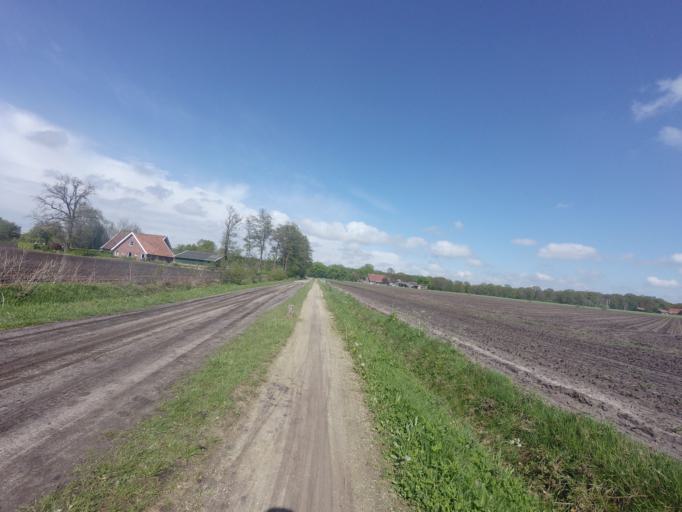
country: NL
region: Overijssel
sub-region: Gemeente Haaksbergen
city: Haaksbergen
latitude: 52.1661
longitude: 6.7991
